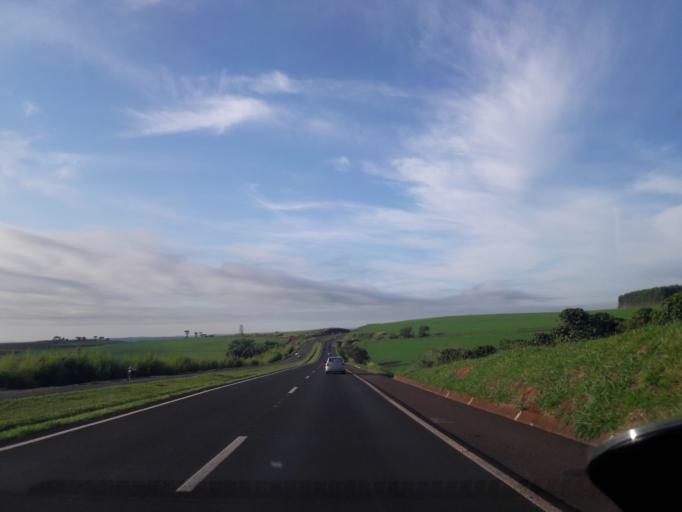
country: BR
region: Parana
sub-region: Rolandia
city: Rolandia
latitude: -23.3073
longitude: -51.3303
